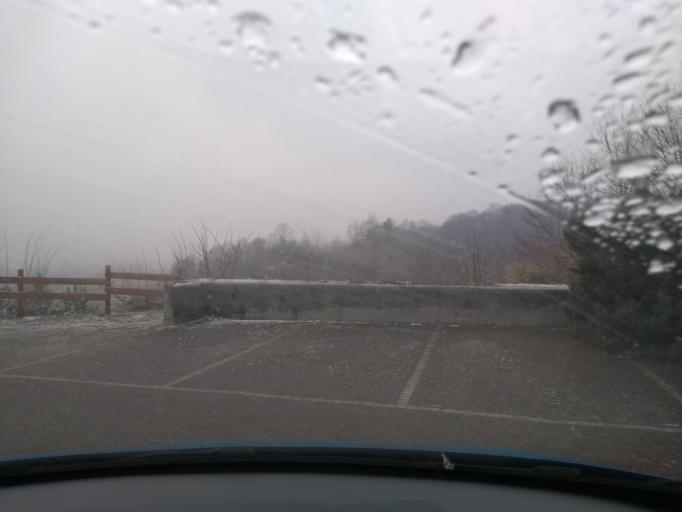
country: IT
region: Piedmont
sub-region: Provincia di Torino
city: Balangero
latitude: 45.2772
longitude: 7.5213
